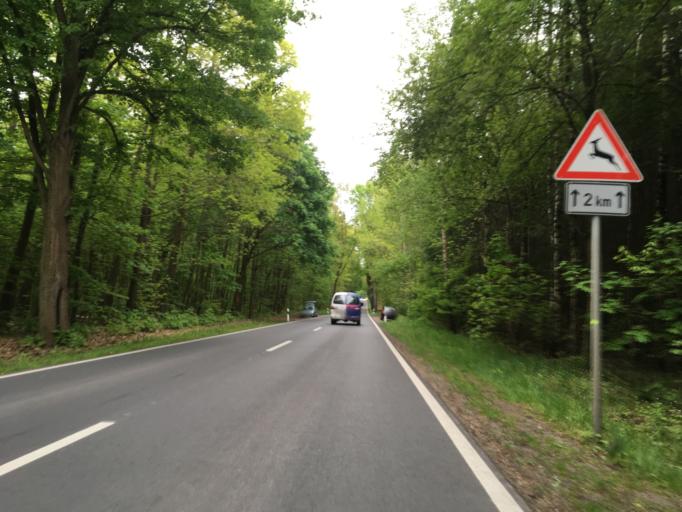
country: DE
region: Brandenburg
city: Bernau bei Berlin
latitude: 52.6292
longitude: 13.6117
